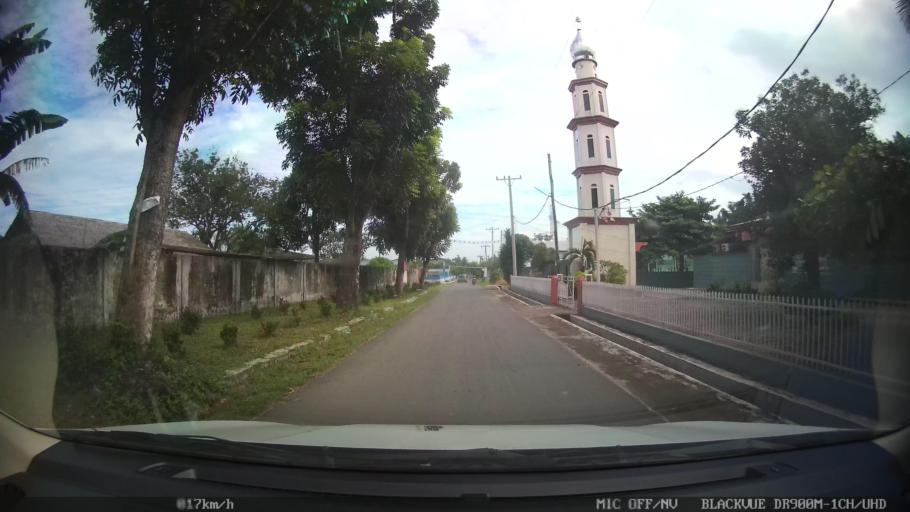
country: ID
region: North Sumatra
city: Sunggal
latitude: 3.5869
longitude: 98.5796
